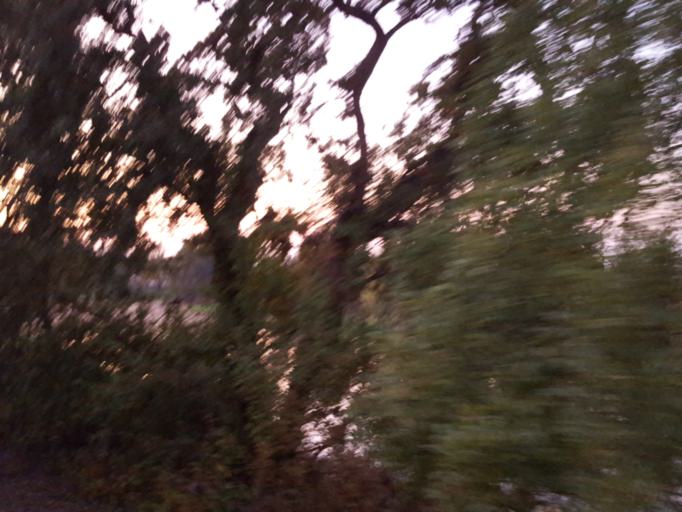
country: US
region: California
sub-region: Yolo County
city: Woodland
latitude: 38.6770
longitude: -121.6413
